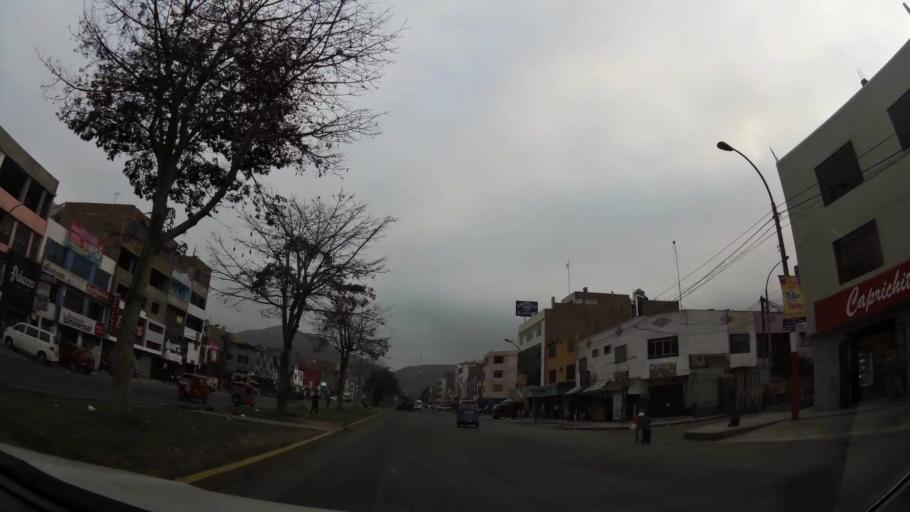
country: PE
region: Lima
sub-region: Lima
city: Independencia
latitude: -12.0065
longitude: -77.0078
